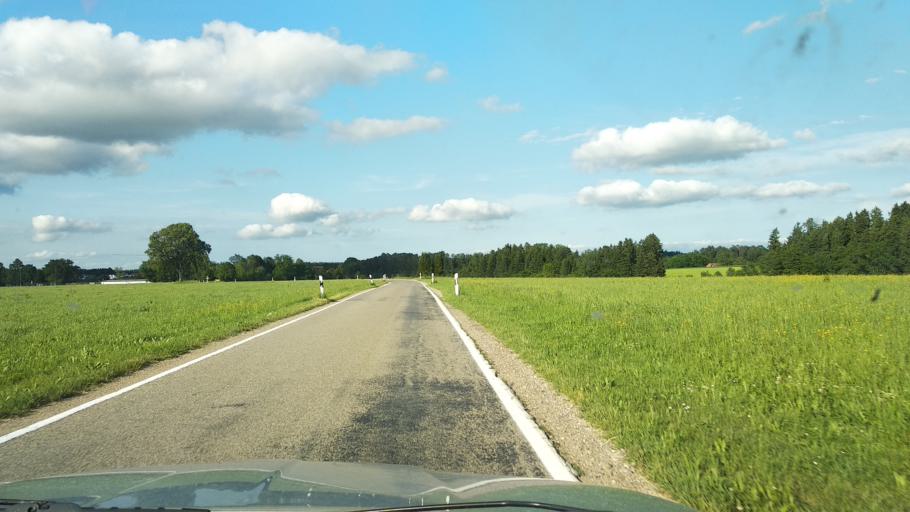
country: DE
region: Baden-Wuerttemberg
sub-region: Tuebingen Region
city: Rot an der Rot
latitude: 47.9679
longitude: 10.0428
